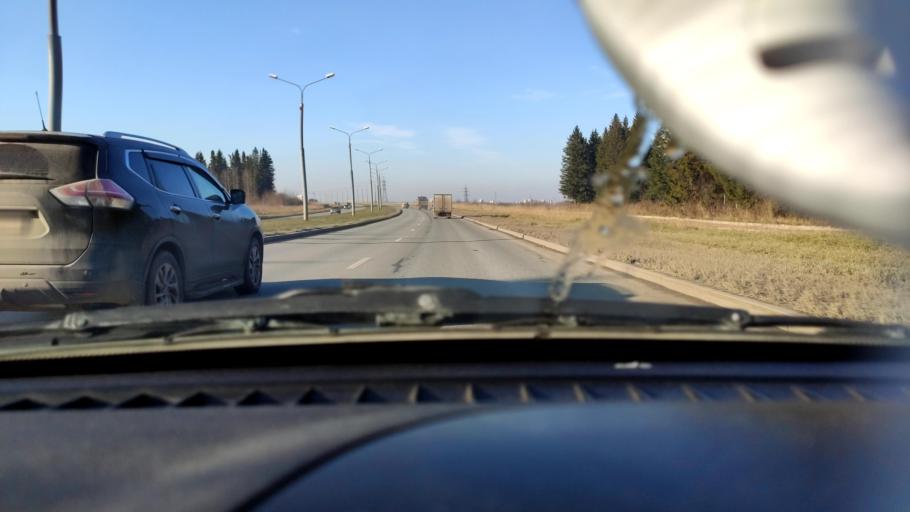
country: RU
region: Perm
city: Perm
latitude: 58.0041
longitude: 56.3701
